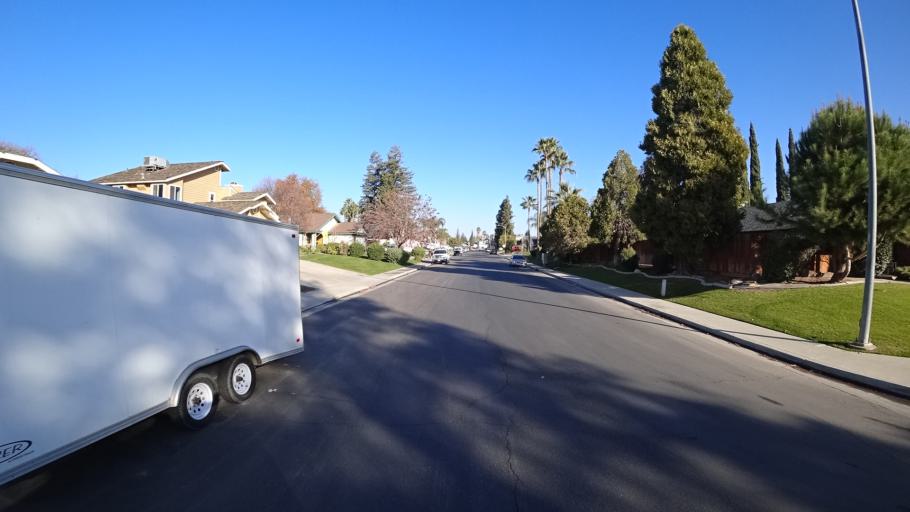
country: US
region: California
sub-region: Kern County
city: Rosedale
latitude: 35.3487
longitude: -119.1494
